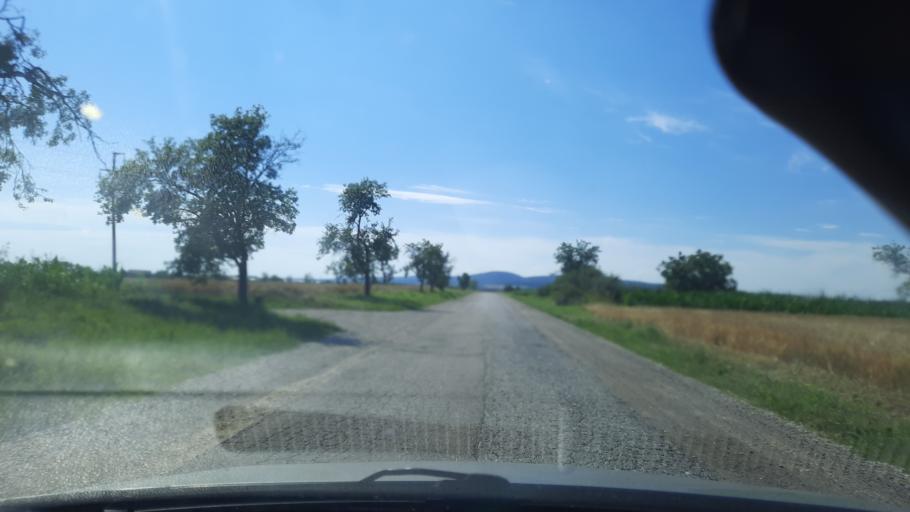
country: RS
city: Cortanovci
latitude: 45.1127
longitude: 19.9671
